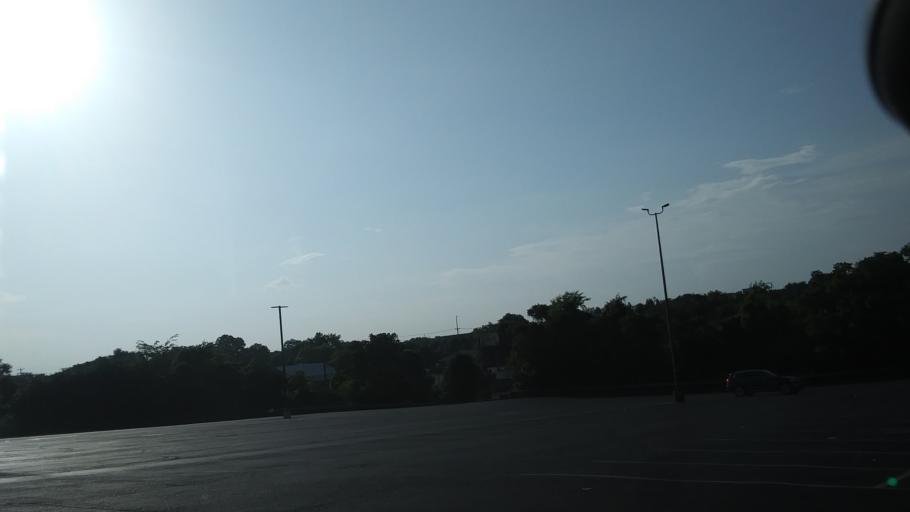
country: US
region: Tennessee
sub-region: Davidson County
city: Belle Meade
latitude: 36.1477
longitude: -86.8625
